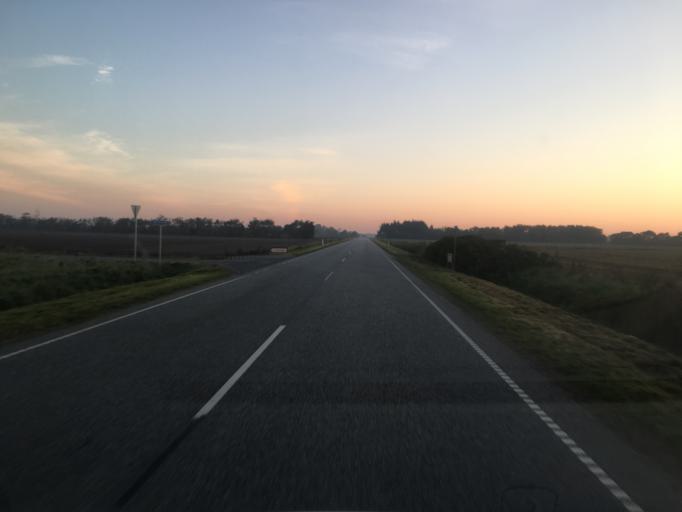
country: DK
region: South Denmark
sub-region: Tonder Kommune
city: Logumkloster
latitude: 55.0110
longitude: 9.0488
